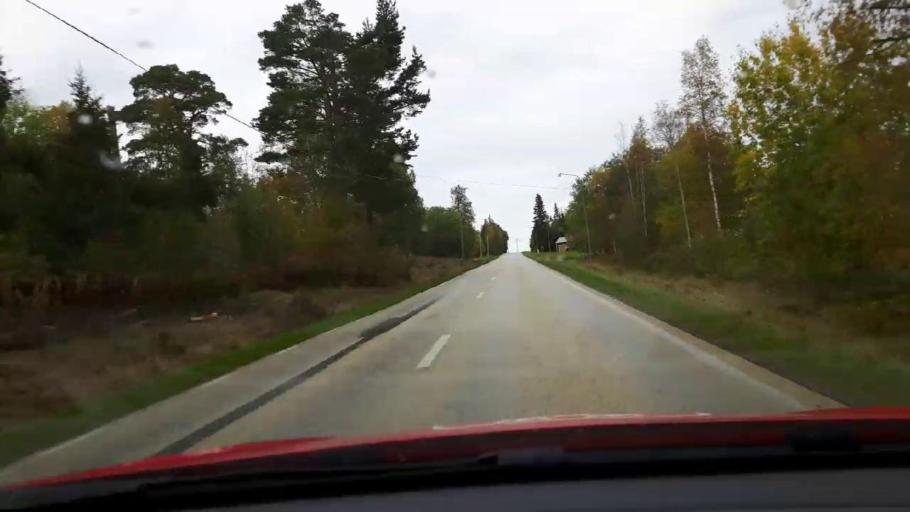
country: SE
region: Jaemtland
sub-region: Bergs Kommun
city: Hoverberg
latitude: 62.9837
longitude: 14.3422
